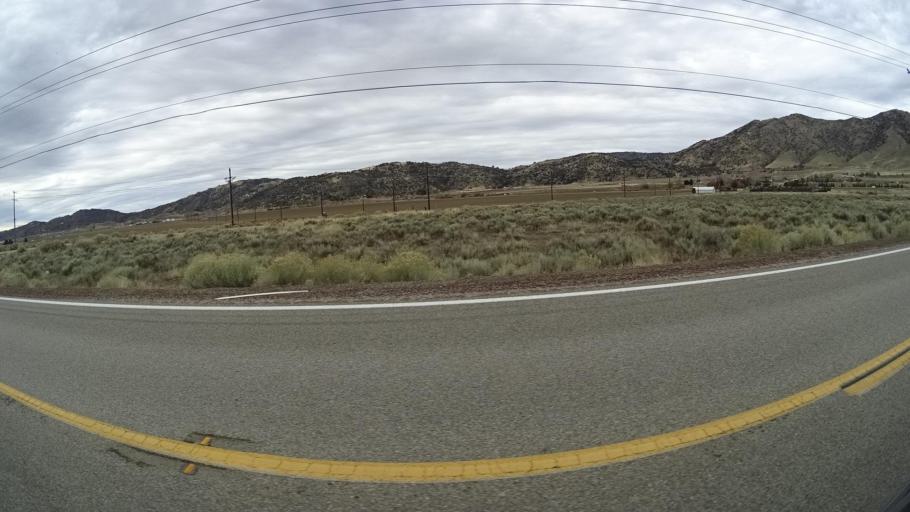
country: US
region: California
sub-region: Kern County
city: Bear Valley Springs
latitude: 35.1247
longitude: -118.5733
